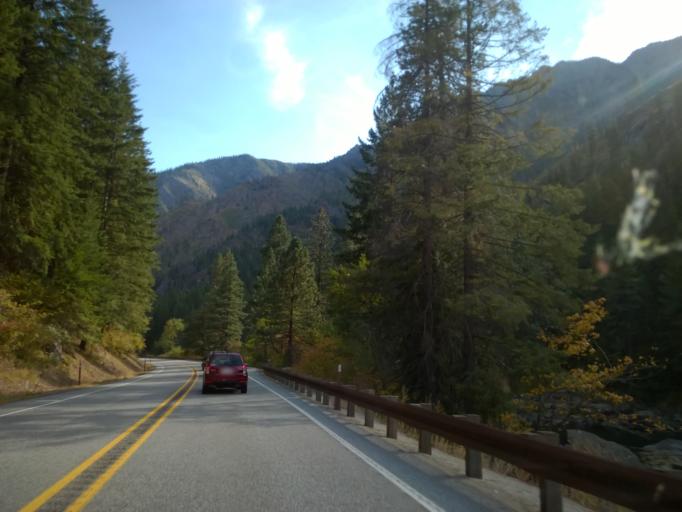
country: US
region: Washington
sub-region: Chelan County
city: Leavenworth
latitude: 47.5970
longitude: -120.7136
